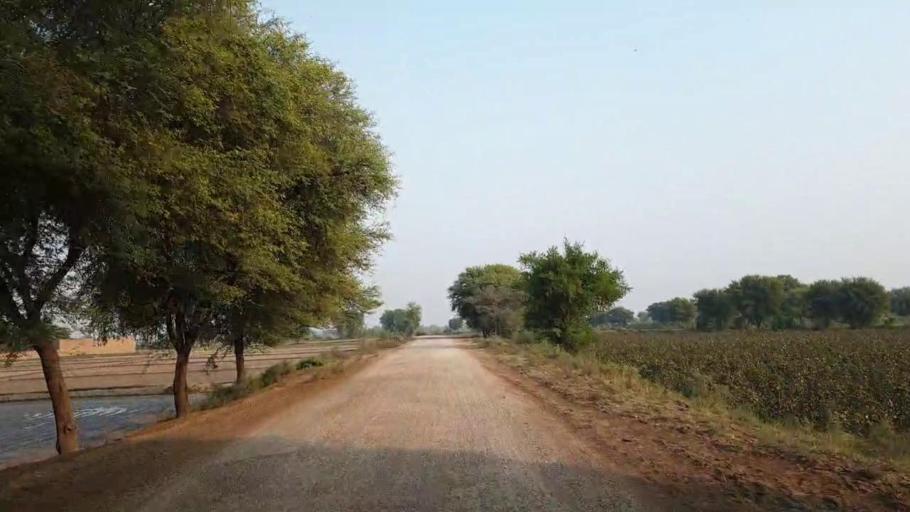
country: PK
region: Sindh
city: Bhan
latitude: 26.5014
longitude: 67.7621
